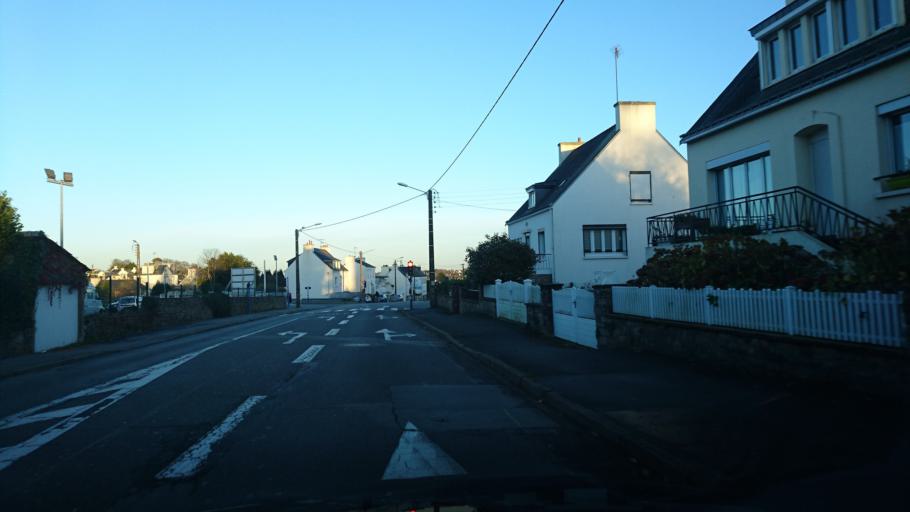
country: FR
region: Brittany
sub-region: Departement du Finistere
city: Quimperle
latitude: 47.8716
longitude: -3.5620
